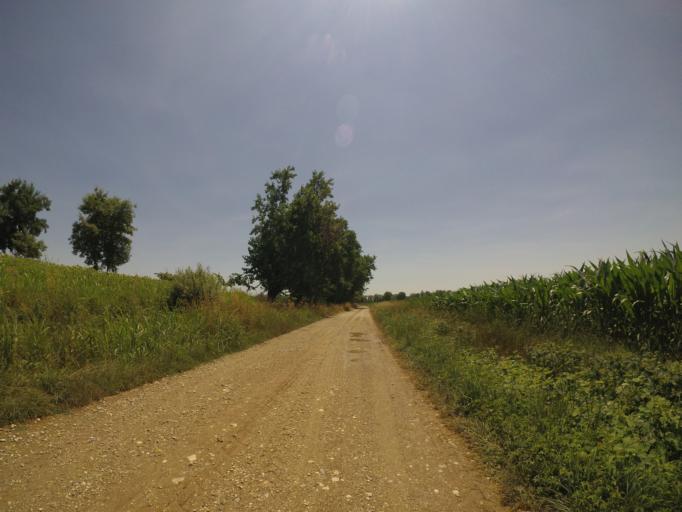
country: IT
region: Friuli Venezia Giulia
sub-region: Provincia di Udine
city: Talmassons
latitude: 45.9280
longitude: 13.0916
